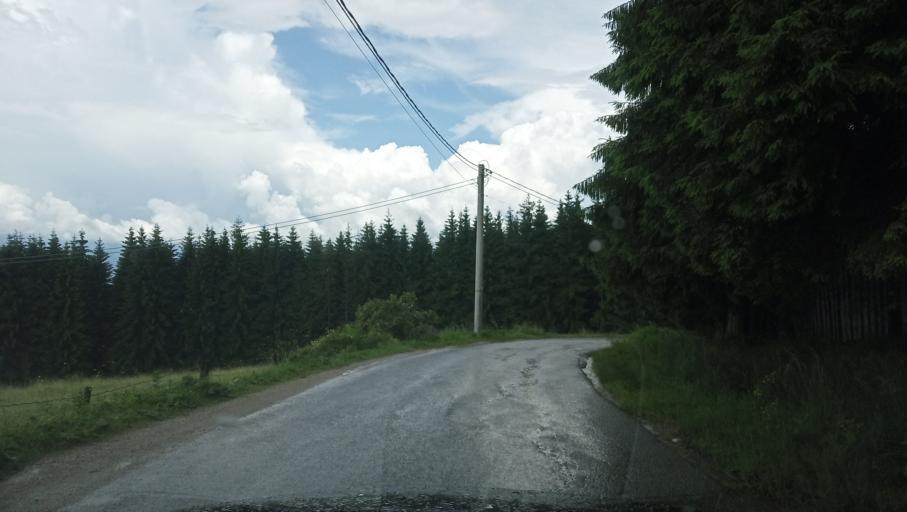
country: RO
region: Hunedoara
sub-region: Oras Petrila
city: Petrila
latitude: 45.3920
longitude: 23.4362
